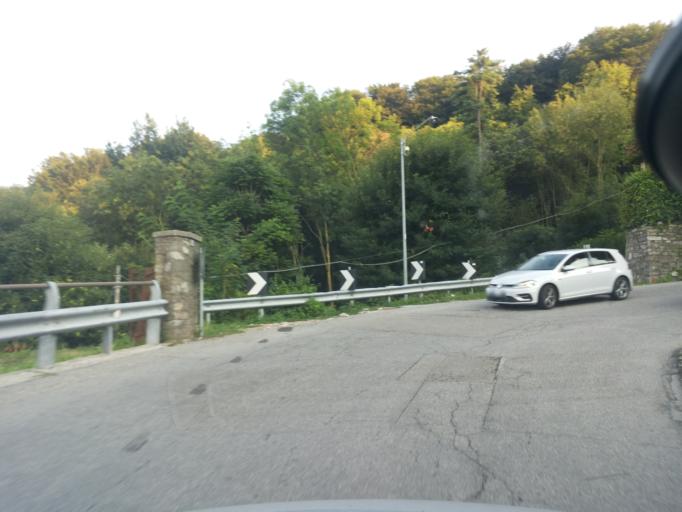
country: IT
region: Piedmont
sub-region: Provincia Verbano-Cusio-Ossola
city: Stresa
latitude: 45.8741
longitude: 8.5465
